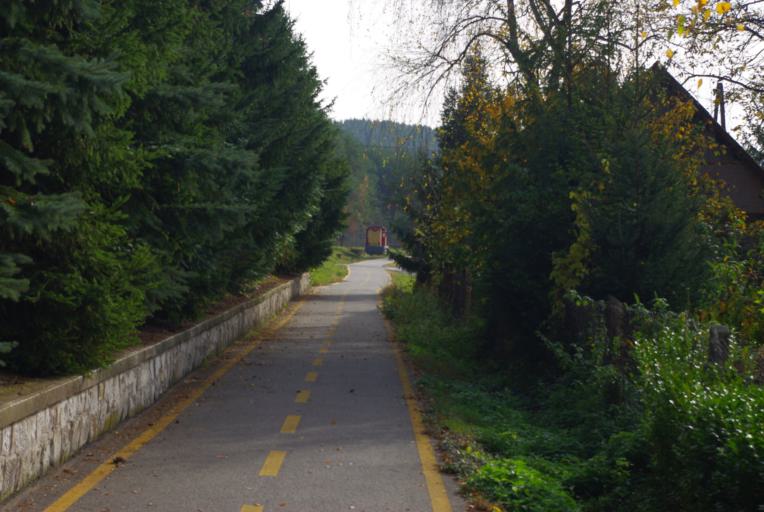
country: HU
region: Borsod-Abauj-Zemplen
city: Gonc
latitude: 48.5126
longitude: 21.4554
